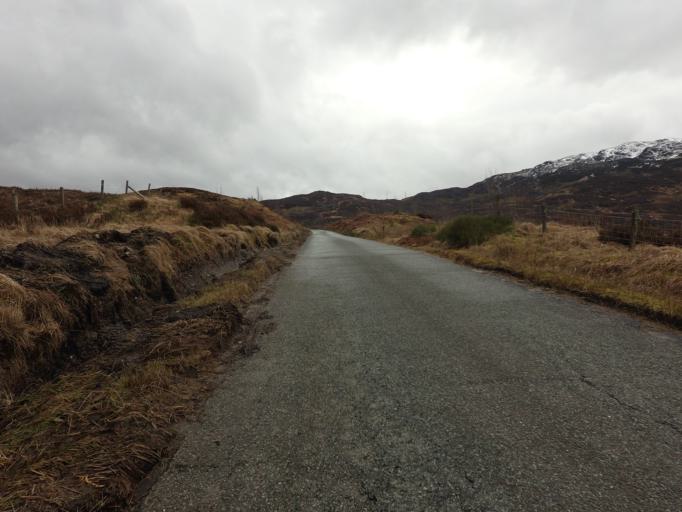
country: GB
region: Scotland
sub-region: West Dunbartonshire
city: Balloch
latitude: 56.2518
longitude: -4.5885
